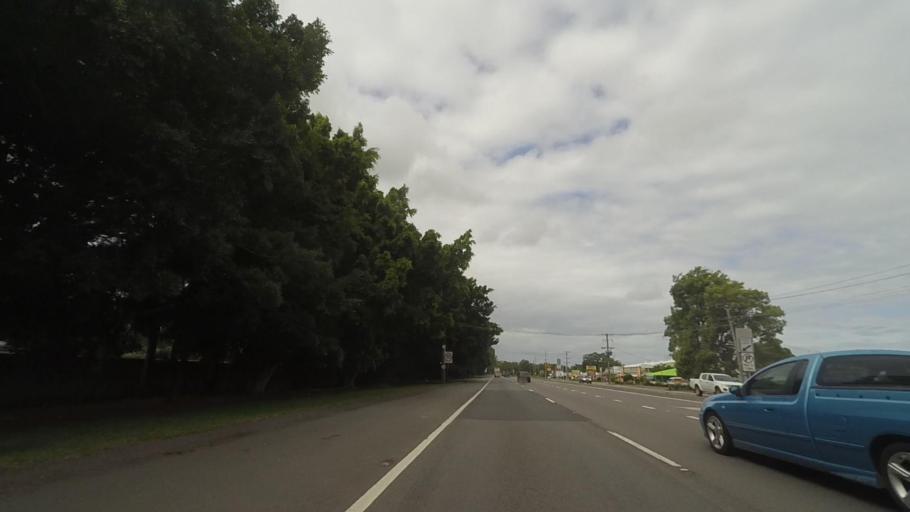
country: AU
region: New South Wales
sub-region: Port Stephens Shire
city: Raymond Terrace
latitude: -32.7852
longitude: 151.7325
